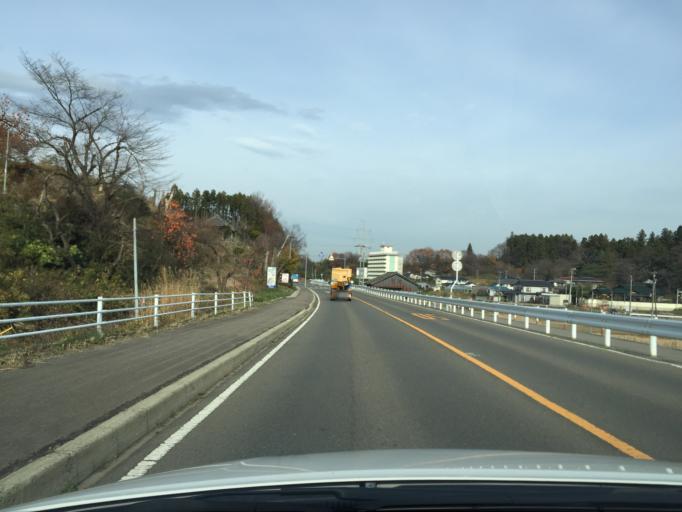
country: JP
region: Fukushima
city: Fukushima-shi
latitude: 37.6692
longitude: 140.4646
